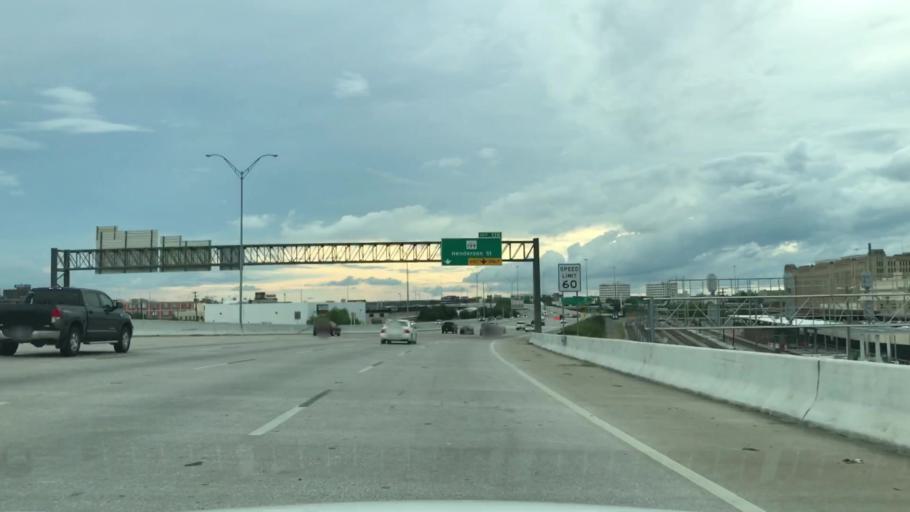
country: US
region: Texas
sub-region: Tarrant County
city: Fort Worth
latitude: 32.7449
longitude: -97.3258
